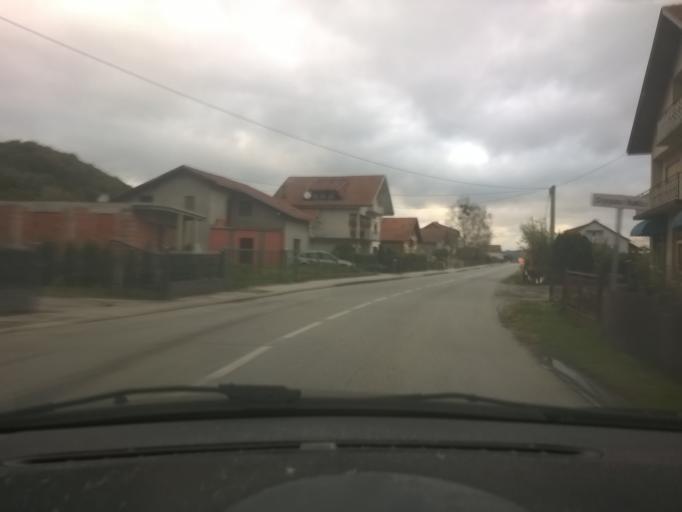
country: HR
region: Zagrebacka
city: Jakovlje
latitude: 45.9821
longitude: 15.8380
